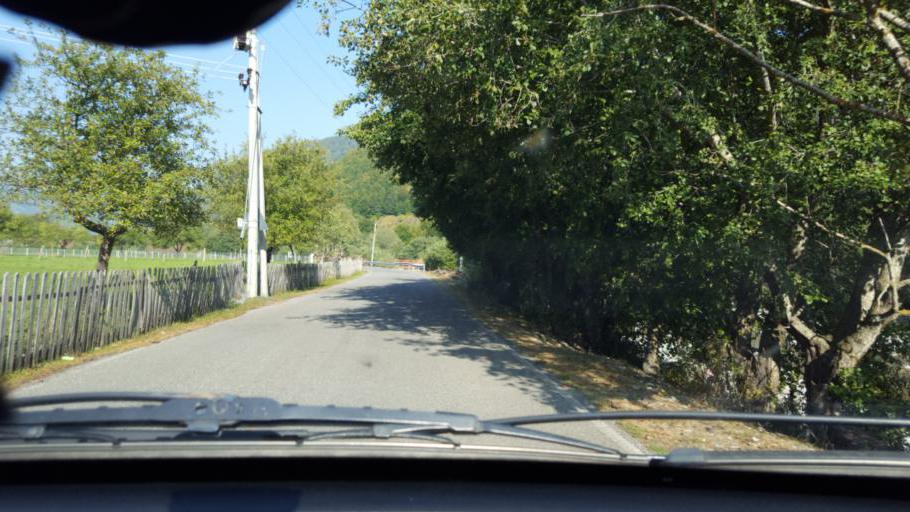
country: ME
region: Andrijevica
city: Andrijevica
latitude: 42.5877
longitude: 19.7115
